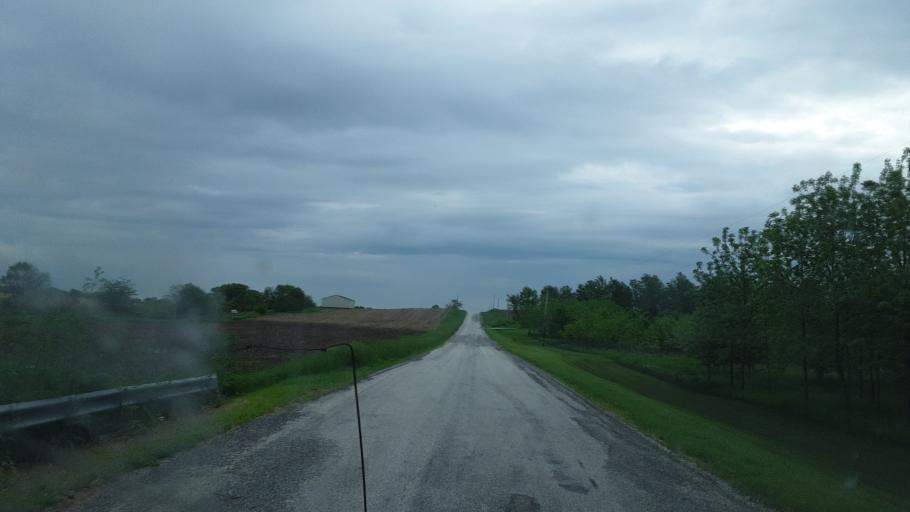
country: US
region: Illinois
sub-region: McDonough County
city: Macomb
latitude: 40.3816
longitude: -90.6076
